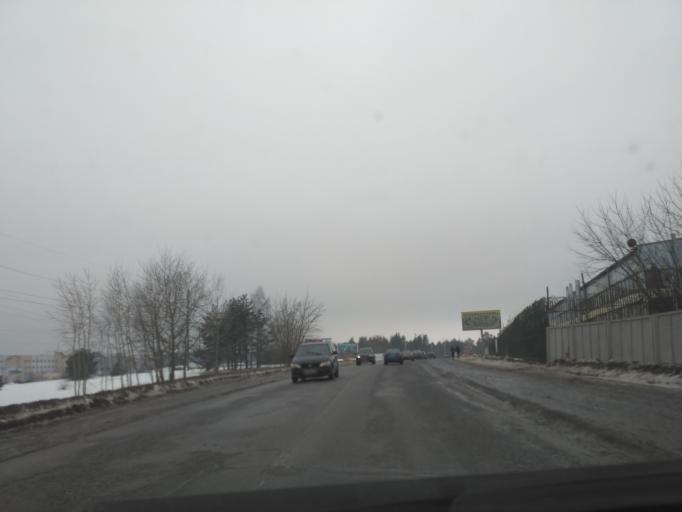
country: BY
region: Minsk
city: Horad Barysaw
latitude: 54.1992
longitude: 28.4902
